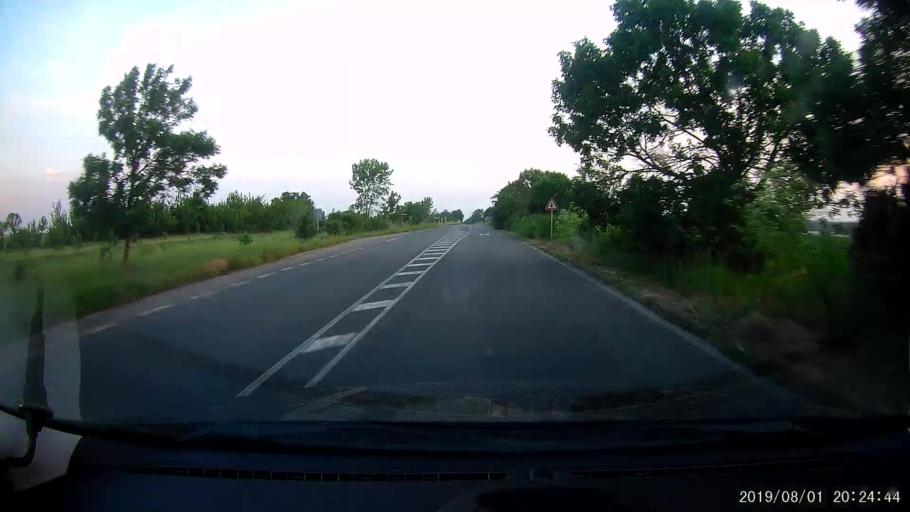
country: BG
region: Yambol
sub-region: Obshtina Elkhovo
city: Elkhovo
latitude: 42.2270
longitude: 26.5918
